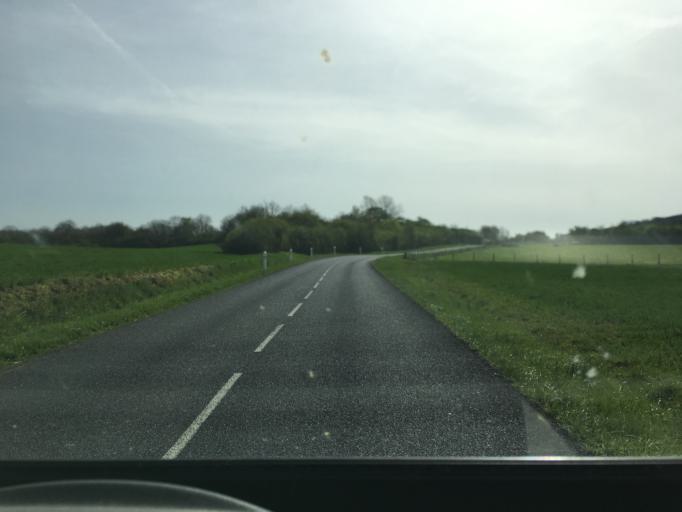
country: FR
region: Lorraine
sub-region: Departement de Meurthe-et-Moselle
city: Dommartin-les-Toul
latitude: 48.6706
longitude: 5.9349
